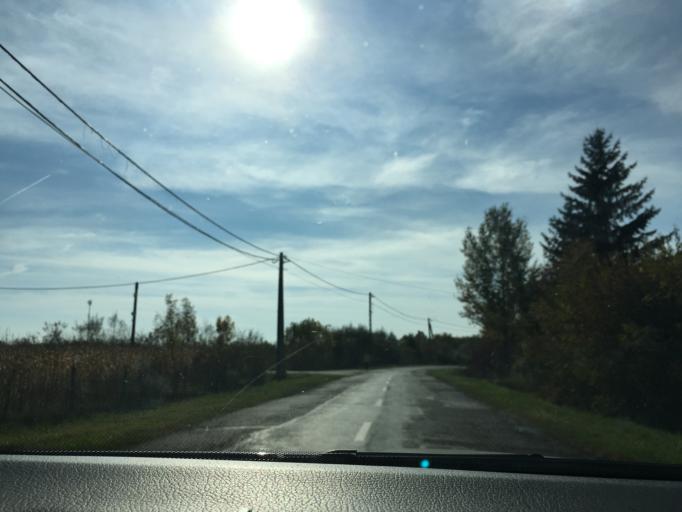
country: HU
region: Hajdu-Bihar
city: Nyirabrany
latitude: 47.5400
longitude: 22.0093
